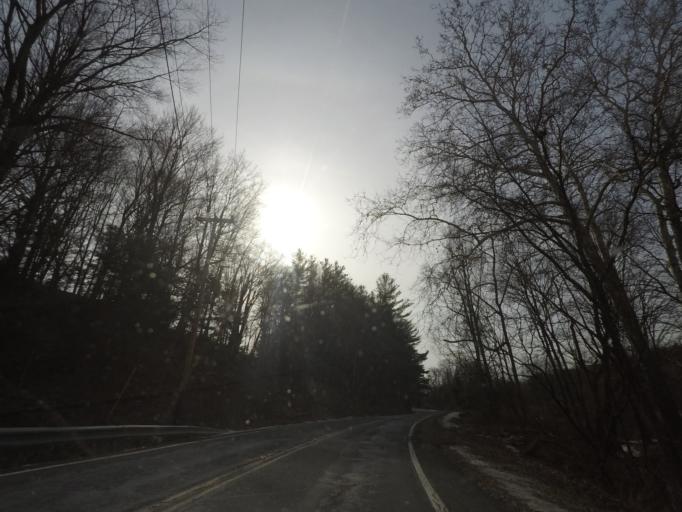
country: US
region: New York
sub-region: Rensselaer County
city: Nassau
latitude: 42.4739
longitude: -73.5759
